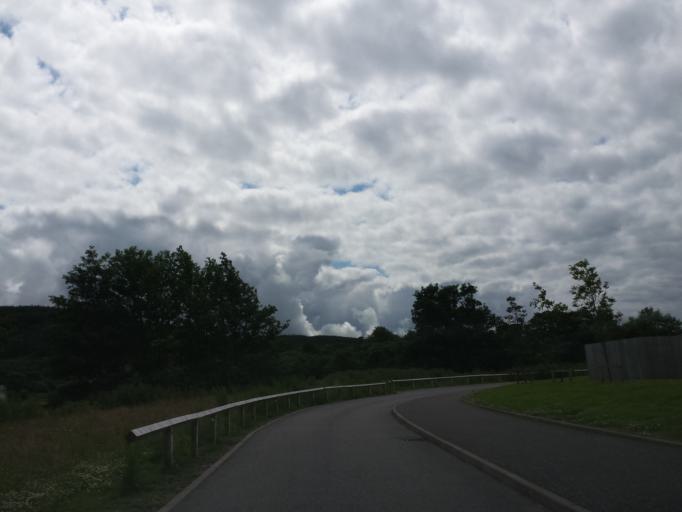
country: GB
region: Scotland
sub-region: Argyll and Bute
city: Oban
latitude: 56.4510
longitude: -5.4419
